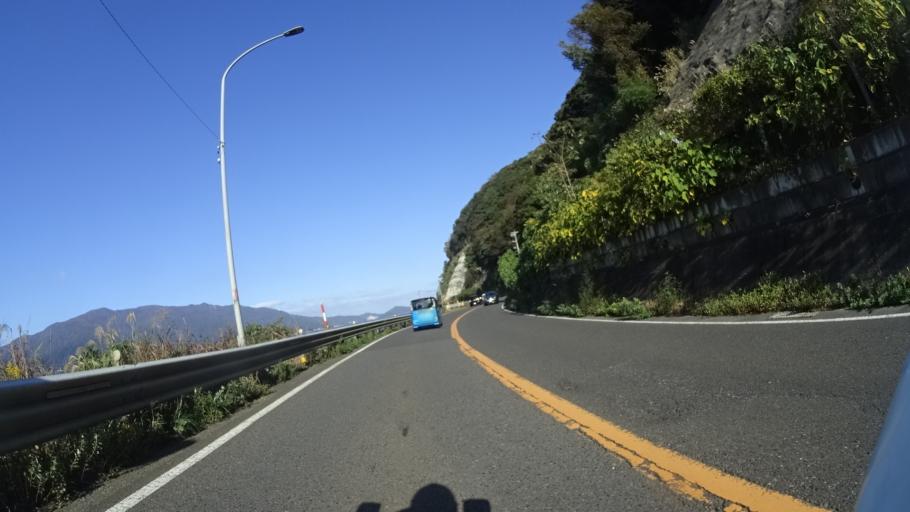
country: JP
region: Fukui
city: Tsuruga
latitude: 35.7004
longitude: 136.0811
